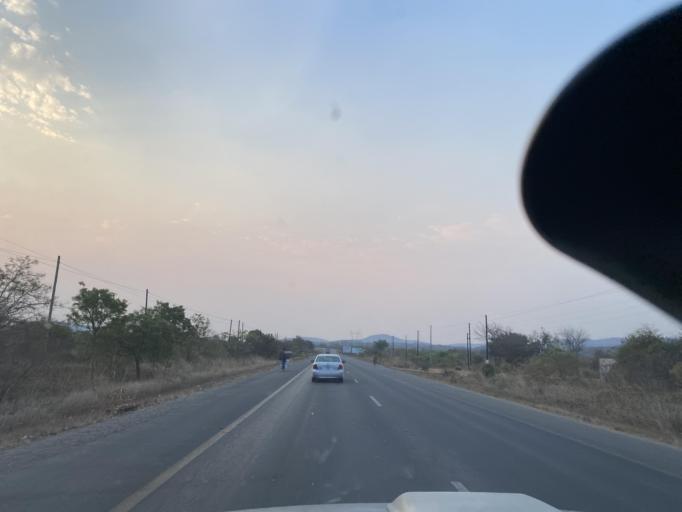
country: ZM
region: Lusaka
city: Kafue
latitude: -15.8280
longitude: 28.2317
